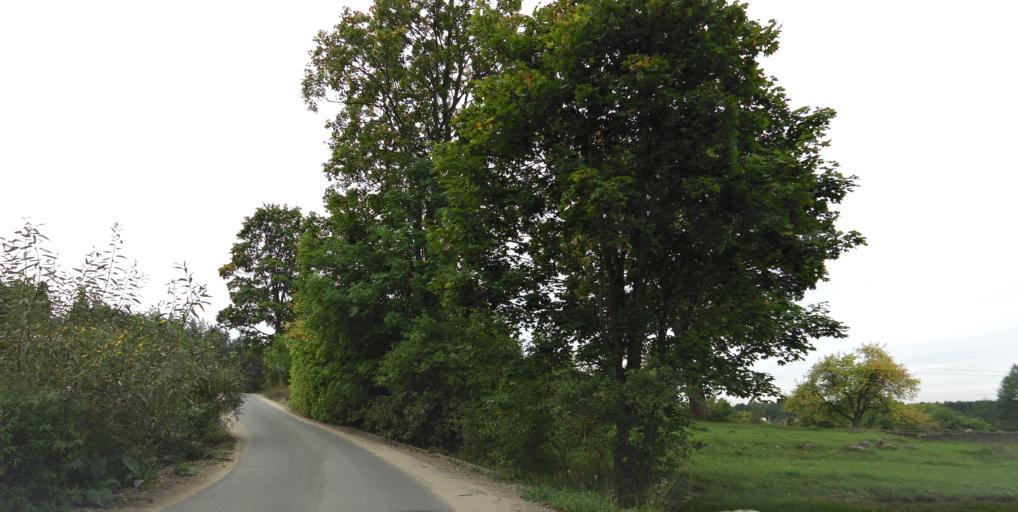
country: LT
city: Grigiskes
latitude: 54.7521
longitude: 25.0291
